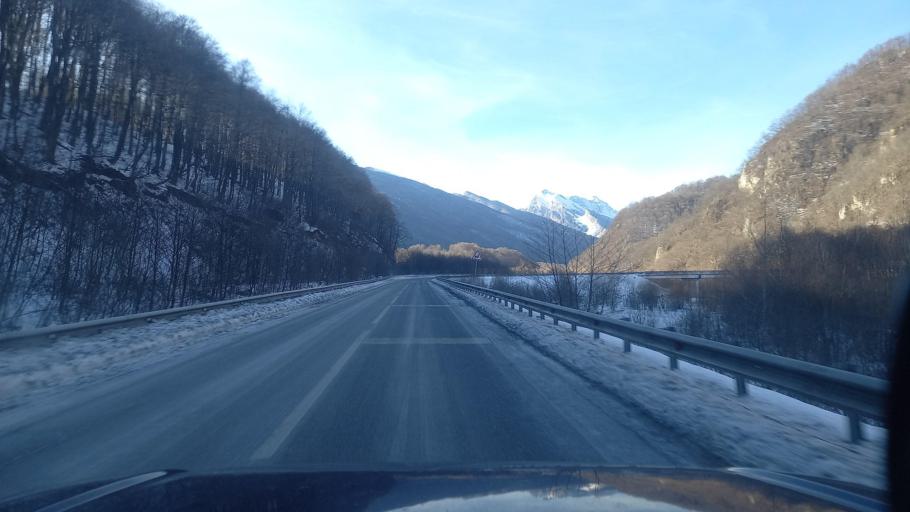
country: RU
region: North Ossetia
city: Gizel'
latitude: 42.9325
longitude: 44.5505
